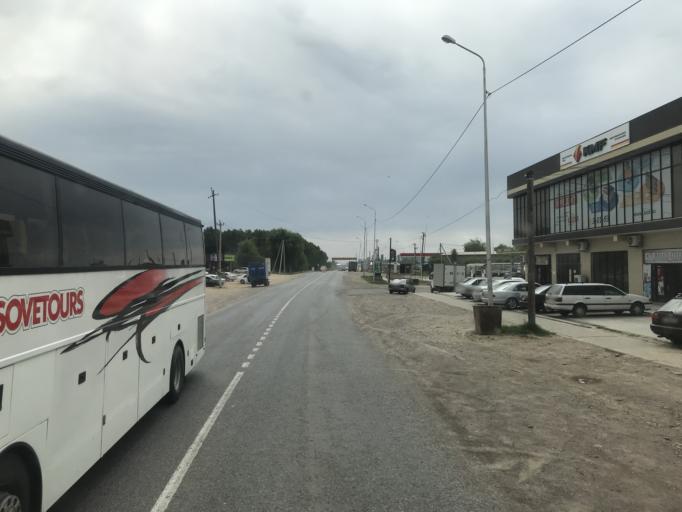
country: UZ
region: Toshkent
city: Yangiyul
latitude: 41.3372
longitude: 68.9481
